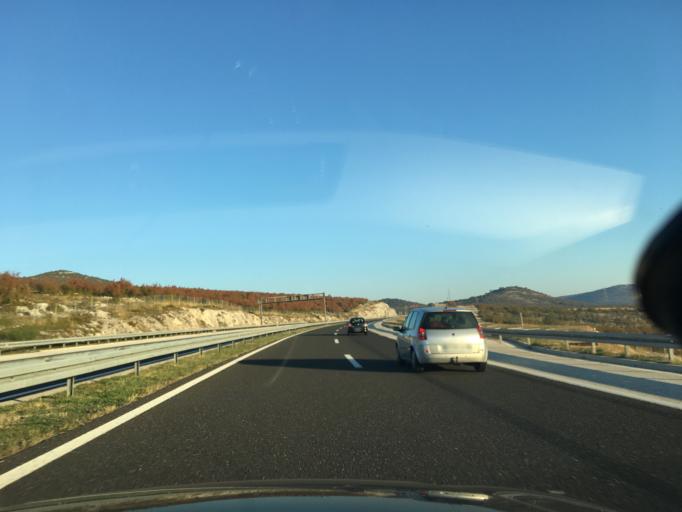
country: HR
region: Splitsko-Dalmatinska
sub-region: Grad Trogir
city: Trogir
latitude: 43.6460
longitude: 16.2009
